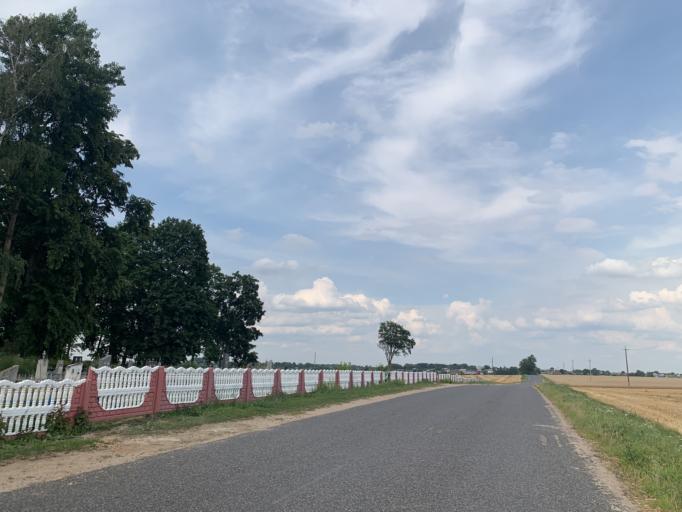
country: BY
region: Minsk
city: Nyasvizh
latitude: 53.1997
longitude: 26.6718
